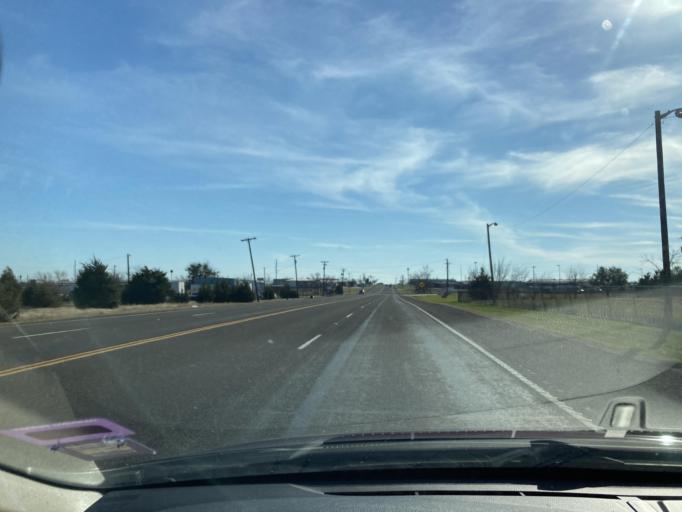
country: US
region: Texas
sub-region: Navarro County
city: Corsicana
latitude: 32.0768
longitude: -96.4531
